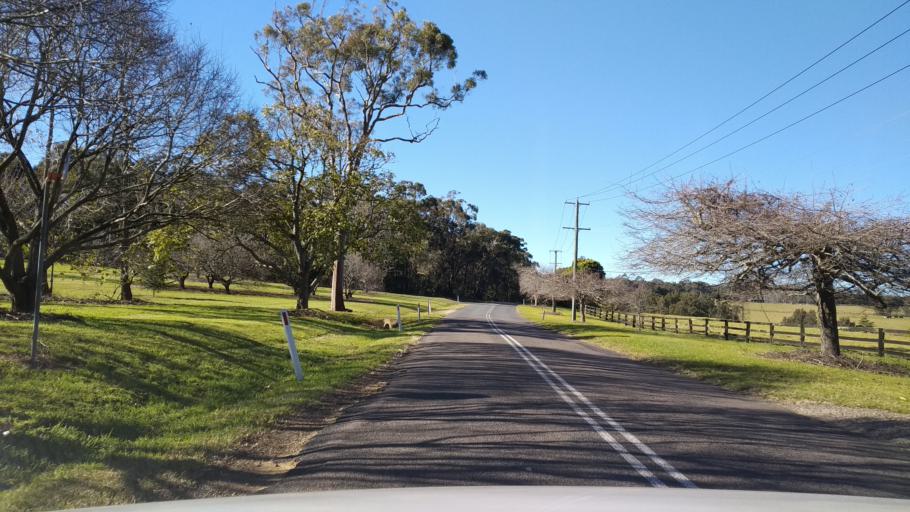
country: AU
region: New South Wales
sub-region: Wyong Shire
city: Little Jilliby
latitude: -33.2438
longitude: 151.2194
